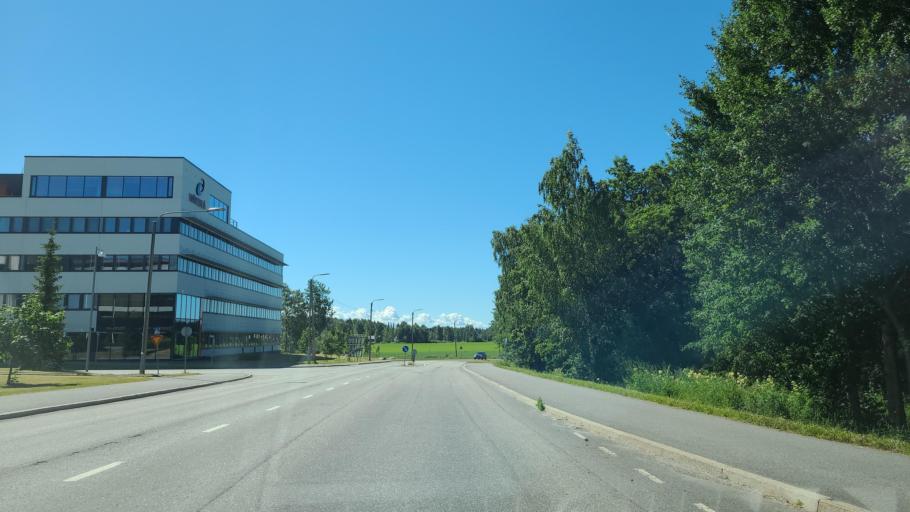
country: FI
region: Ostrobothnia
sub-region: Vaasa
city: Ristinummi
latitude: 63.0575
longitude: 21.7314
